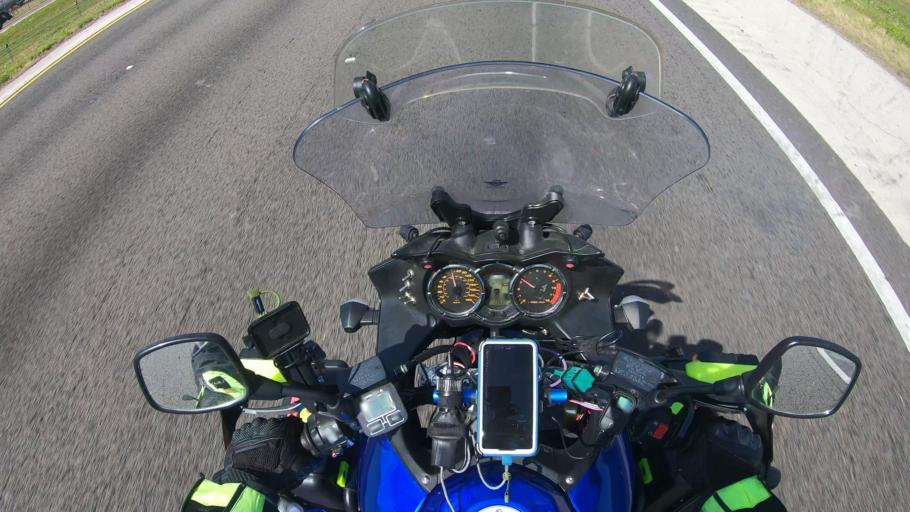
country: US
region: Florida
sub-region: Manatee County
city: Ellenton
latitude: 27.5453
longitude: -82.5116
